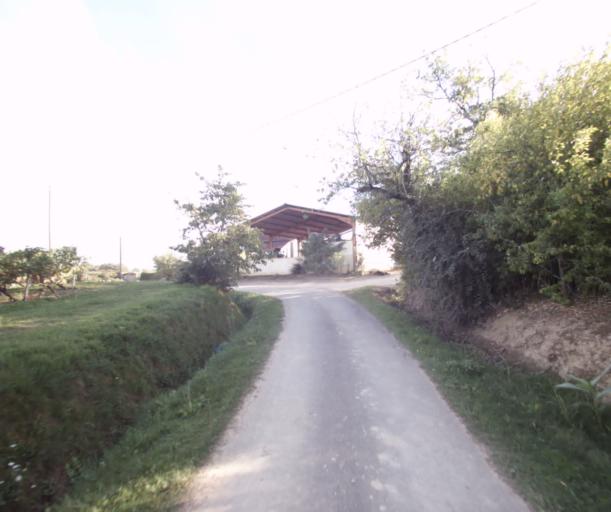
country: FR
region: Midi-Pyrenees
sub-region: Departement du Gers
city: Eauze
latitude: 43.8471
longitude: 0.0336
